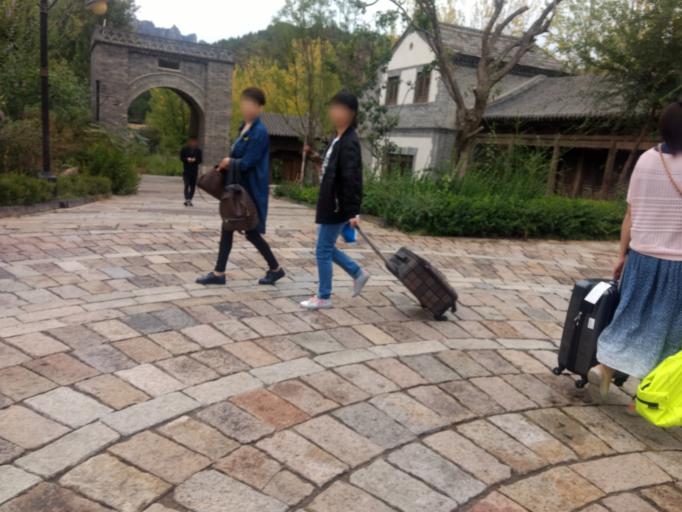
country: CN
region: Beijing
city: Xinchengzi
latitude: 40.6441
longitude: 117.2621
